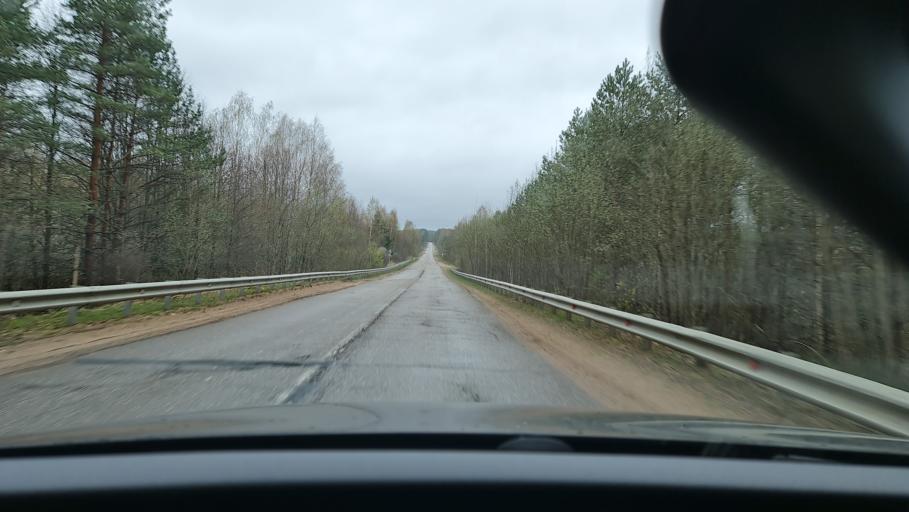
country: RU
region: Novgorod
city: Demyansk
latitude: 57.6597
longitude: 32.5100
